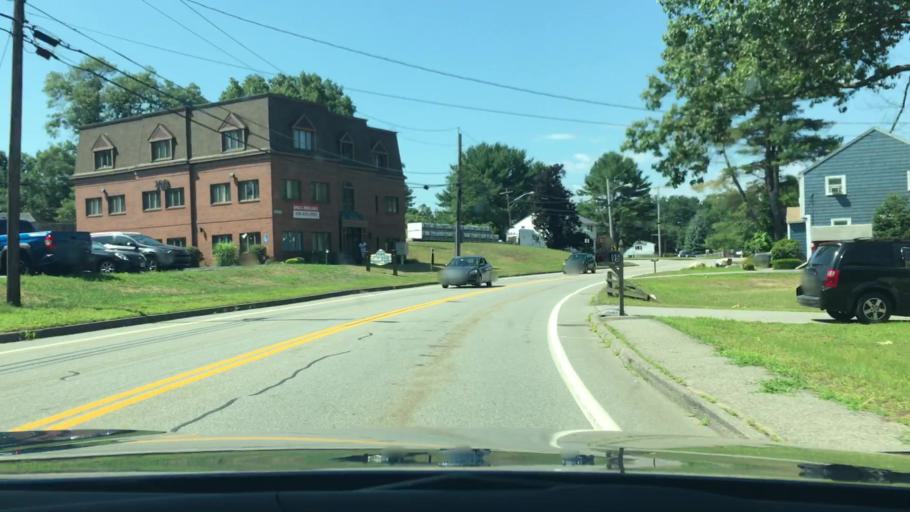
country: US
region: Massachusetts
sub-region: Middlesex County
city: Billerica
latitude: 42.5737
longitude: -71.2897
